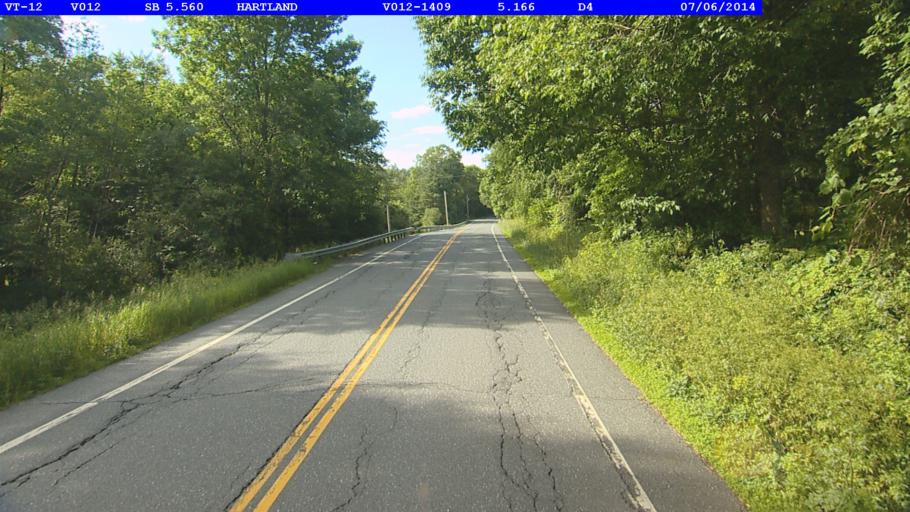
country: US
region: Vermont
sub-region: Windsor County
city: Woodstock
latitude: 43.5921
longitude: -72.4491
